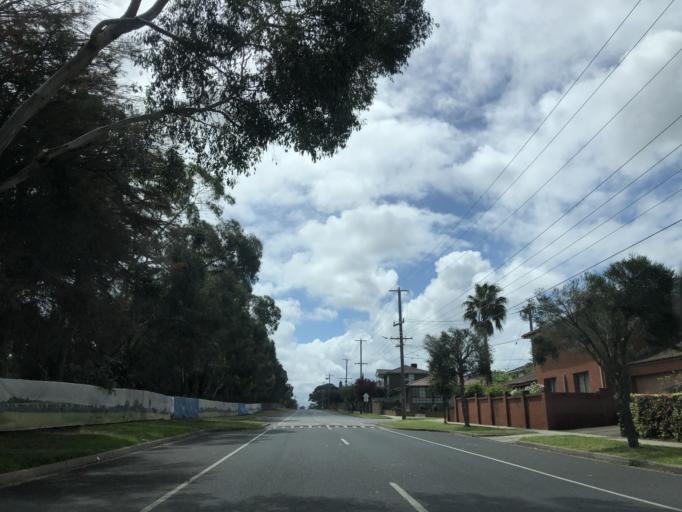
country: AU
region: Victoria
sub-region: Monash
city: Oakleigh South
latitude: -37.9357
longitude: 145.0931
